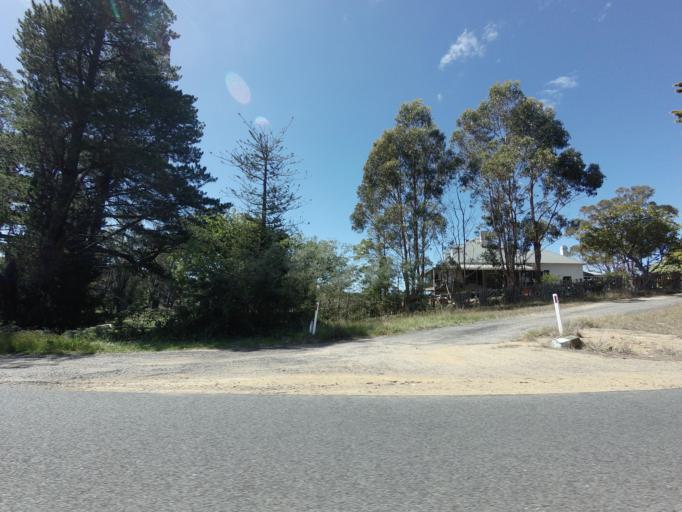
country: AU
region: Tasmania
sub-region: Break O'Day
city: St Helens
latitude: -41.6665
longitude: 148.2845
